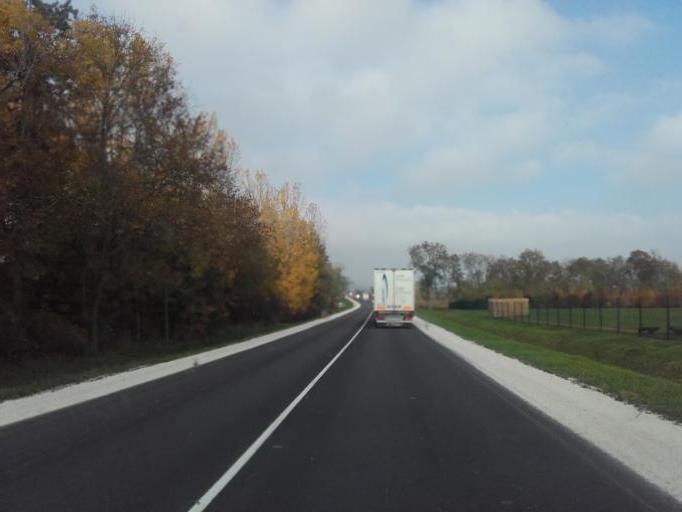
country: FR
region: Bourgogne
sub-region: Departement de la Cote-d'Or
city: Meursault
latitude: 46.9827
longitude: 4.7901
